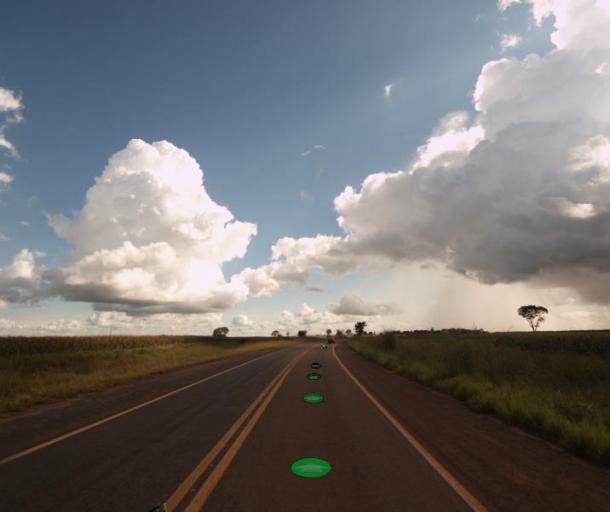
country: BR
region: Goias
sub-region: Itaberai
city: Itaberai
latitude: -15.9846
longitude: -49.6938
